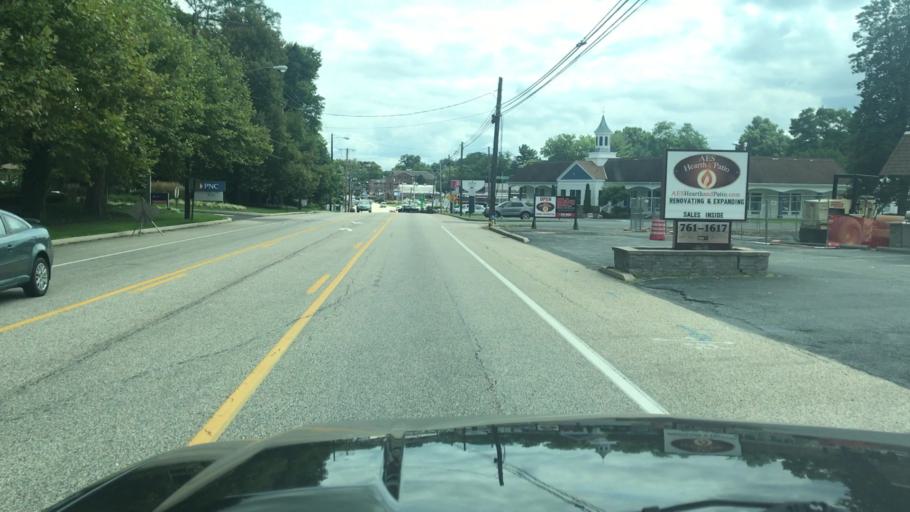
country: US
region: Pennsylvania
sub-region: Cumberland County
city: Shiremanstown
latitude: 40.2379
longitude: -76.9564
